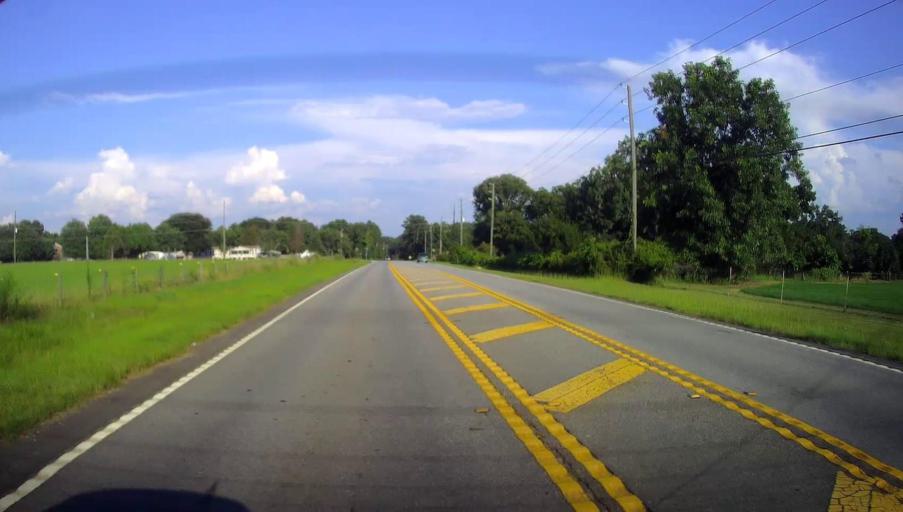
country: US
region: Georgia
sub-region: Houston County
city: Robins Air Force Base
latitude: 32.5011
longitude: -83.6208
